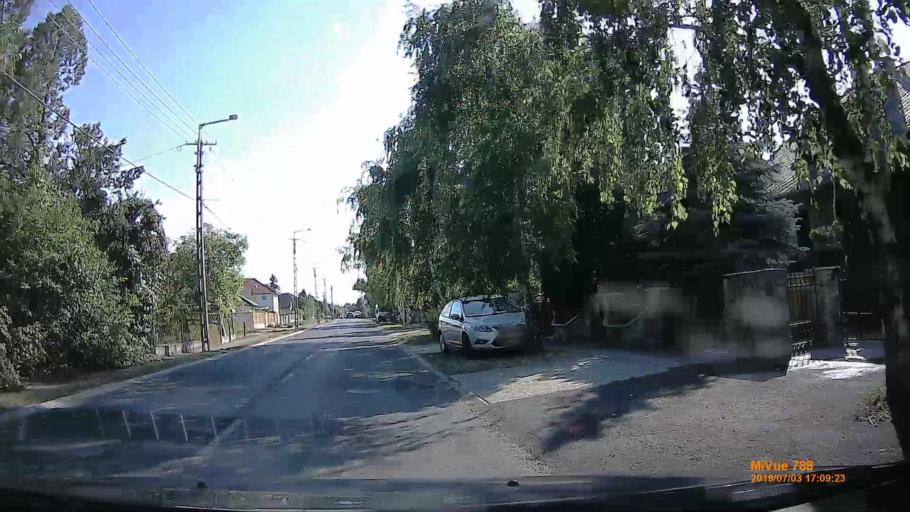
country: HU
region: Gyor-Moson-Sopron
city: Gyor
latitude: 47.7089
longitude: 17.6485
